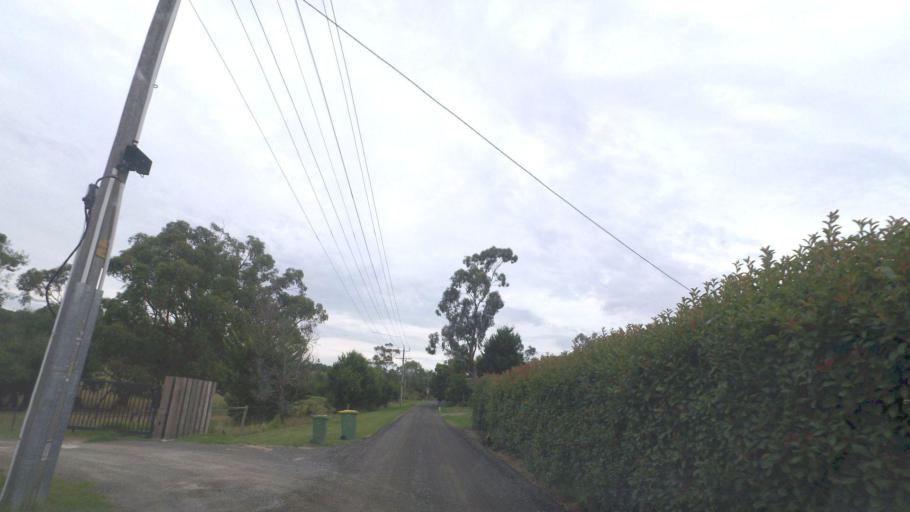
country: AU
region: Victoria
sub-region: Yarra Ranges
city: Lilydale
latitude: -37.7561
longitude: 145.3752
